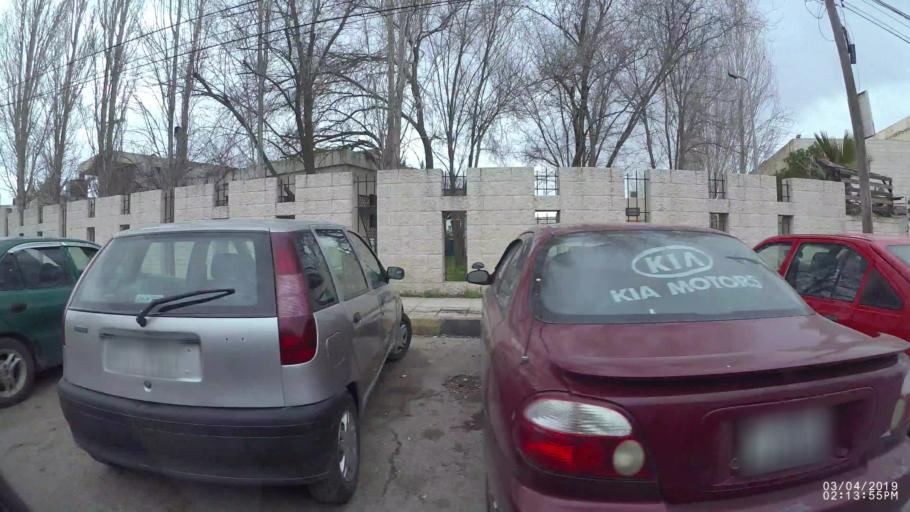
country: JO
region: Amman
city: Wadi as Sir
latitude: 31.9455
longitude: 35.8317
